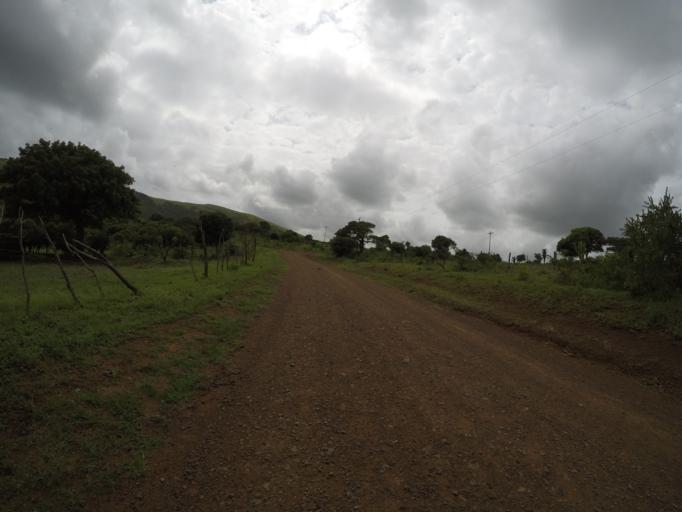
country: ZA
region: KwaZulu-Natal
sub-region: uThungulu District Municipality
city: Empangeni
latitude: -28.6134
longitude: 31.8982
